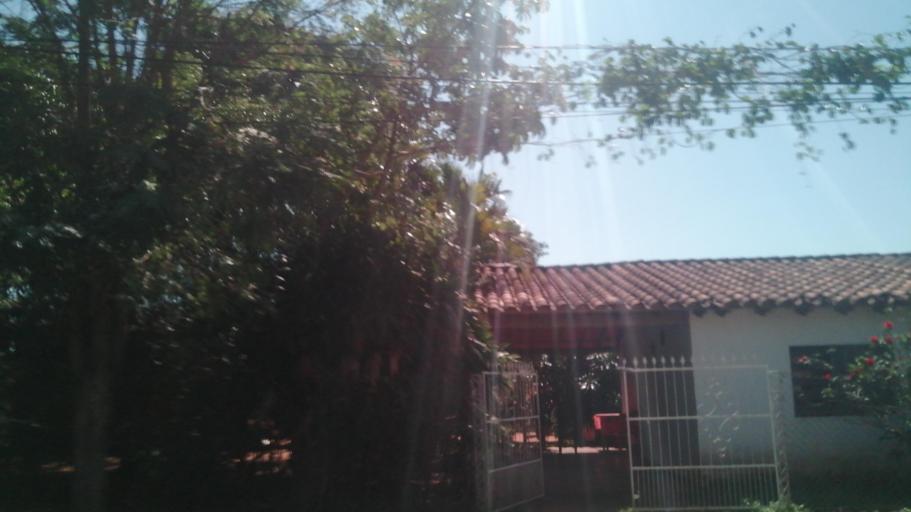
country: PY
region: Misiones
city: San Juan Bautista
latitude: -26.6634
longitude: -57.1533
